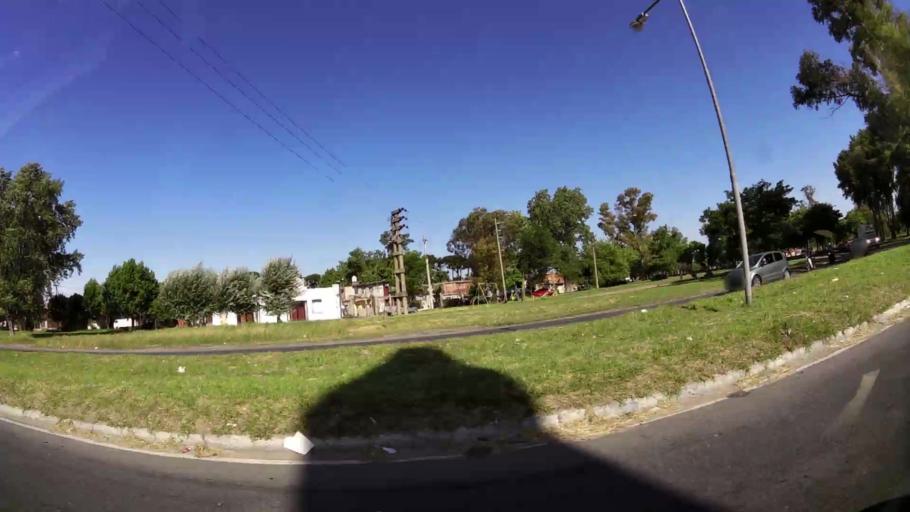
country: AR
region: Buenos Aires
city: Caseros
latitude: -34.5616
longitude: -58.5880
